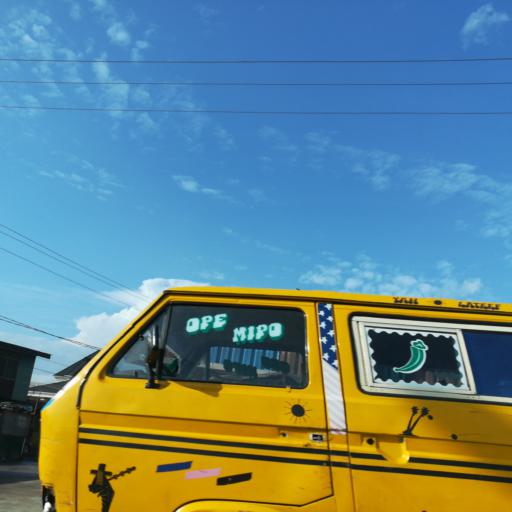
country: NG
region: Lagos
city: Agege
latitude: 6.6158
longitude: 3.3222
